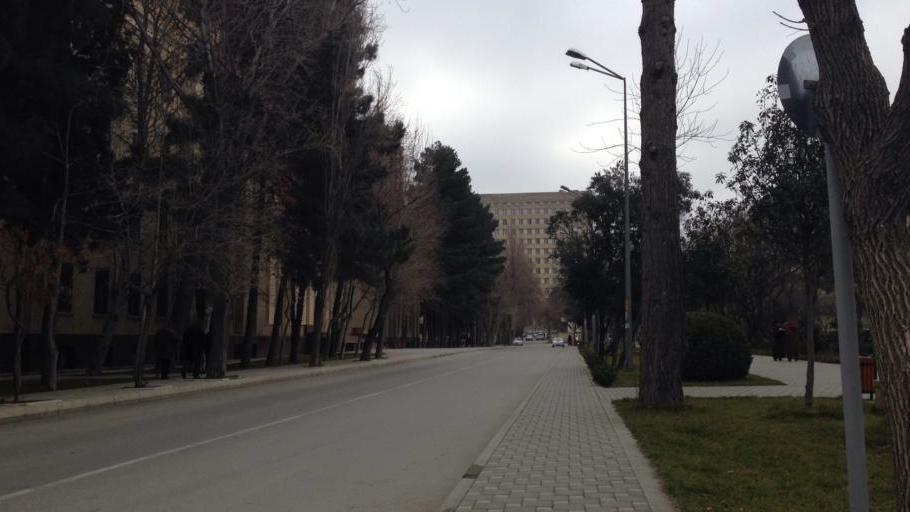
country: AZ
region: Baki
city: Badamdar
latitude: 40.3739
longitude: 49.8132
